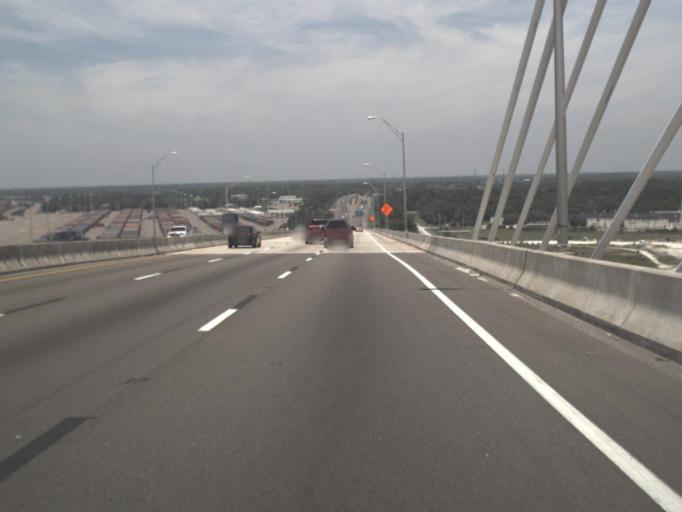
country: US
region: Florida
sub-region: Duval County
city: Jacksonville
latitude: 30.3875
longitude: -81.5581
